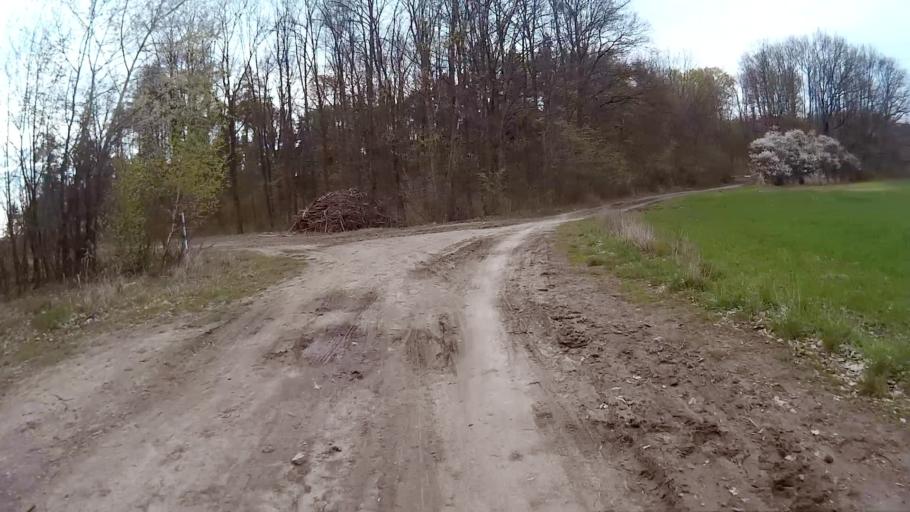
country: CZ
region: South Moravian
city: Kurim
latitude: 49.2465
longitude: 16.5388
